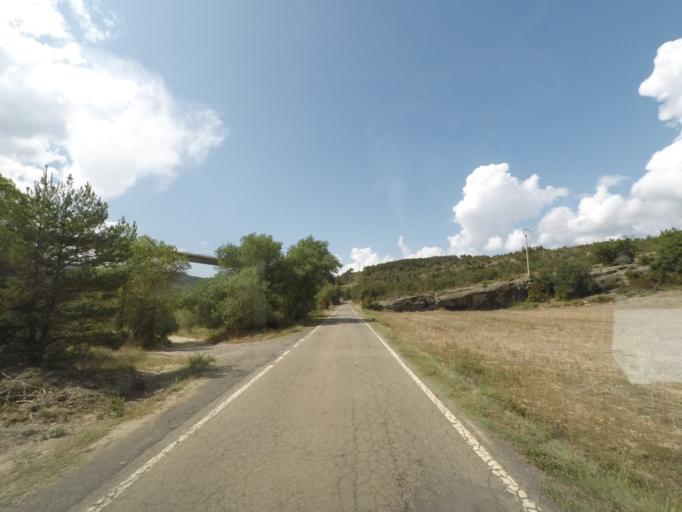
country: ES
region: Aragon
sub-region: Provincia de Huesca
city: Arguis
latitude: 42.4030
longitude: -0.3714
